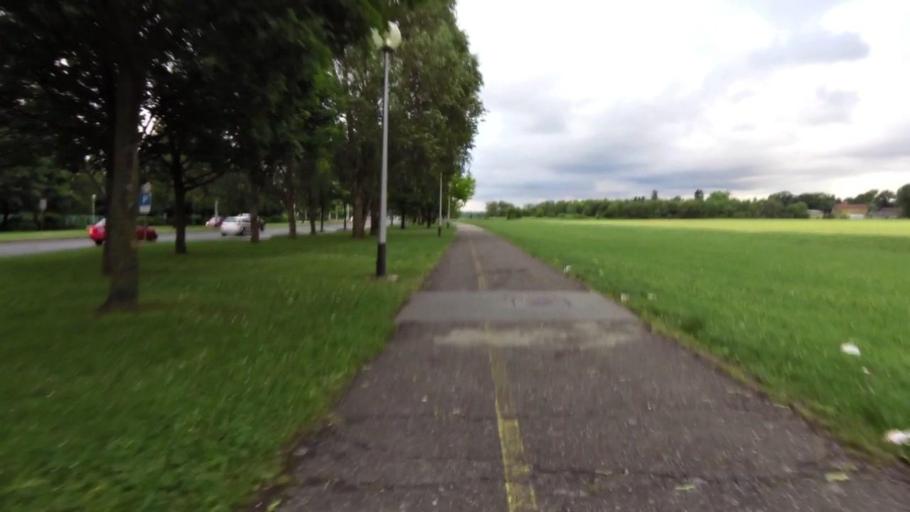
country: HR
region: Grad Zagreb
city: Dubrava
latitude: 45.8334
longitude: 16.0329
